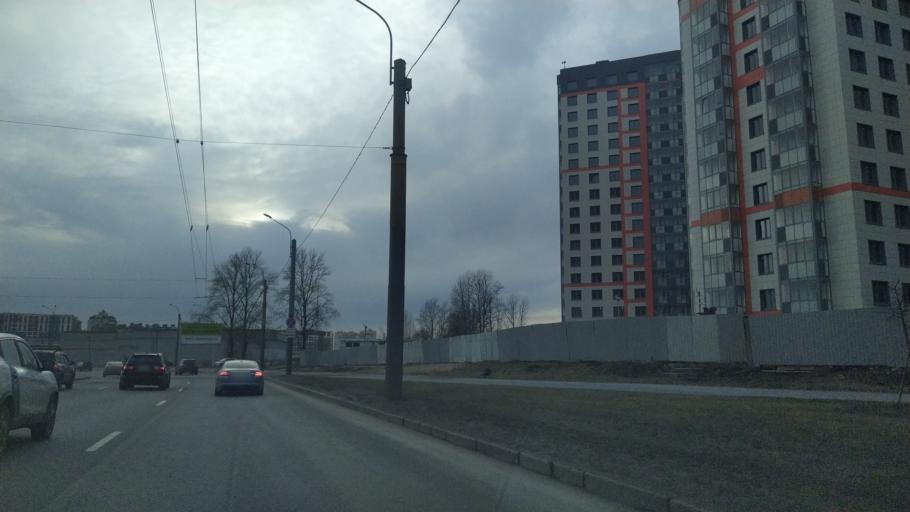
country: RU
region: St.-Petersburg
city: Kushelevka
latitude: 59.9879
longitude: 30.3673
